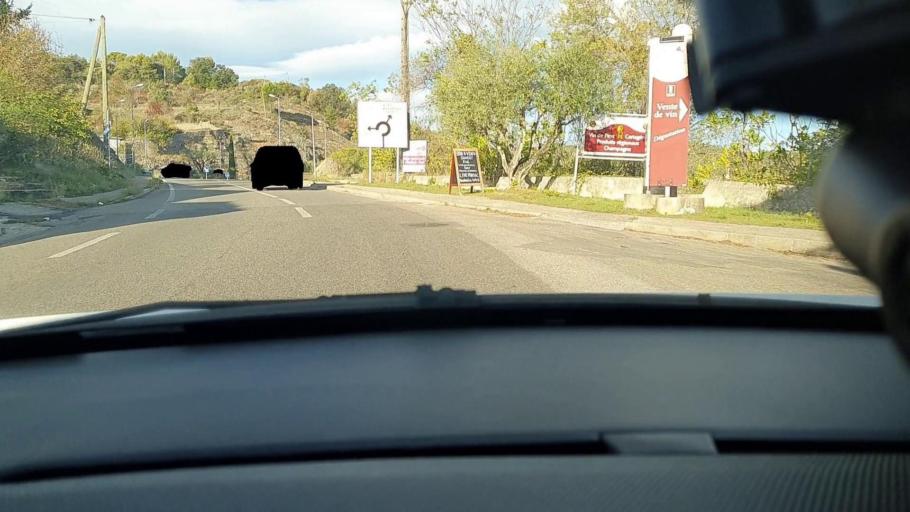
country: FR
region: Languedoc-Roussillon
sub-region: Departement du Gard
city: Saint-Ambroix
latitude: 44.2580
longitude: 4.2063
